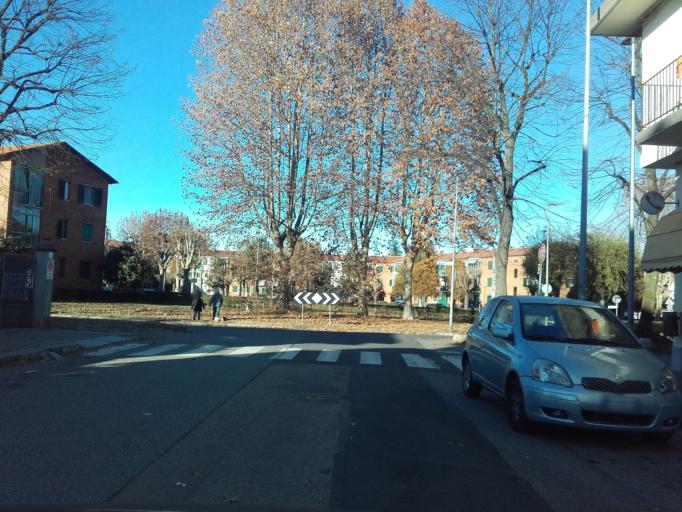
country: IT
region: Piedmont
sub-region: Provincia di Torino
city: Settimo Torinese
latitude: 45.1237
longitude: 7.7099
